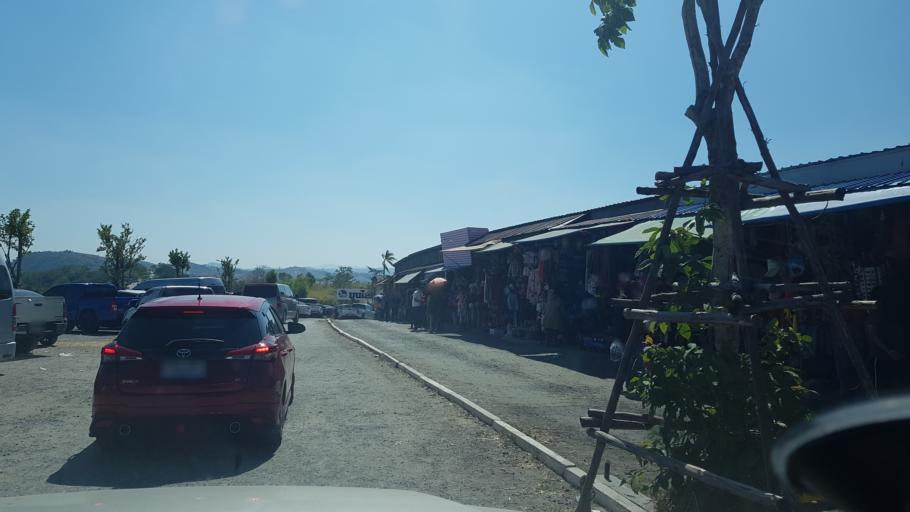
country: TH
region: Phetchabun
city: Khao Kho
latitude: 16.7886
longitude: 101.0513
